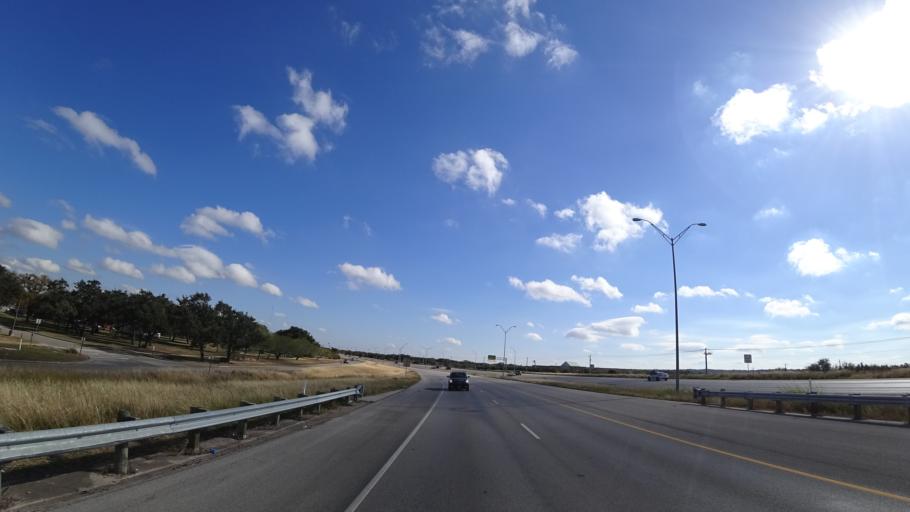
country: US
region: Texas
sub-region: Travis County
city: Shady Hollow
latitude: 30.2166
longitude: -97.8436
